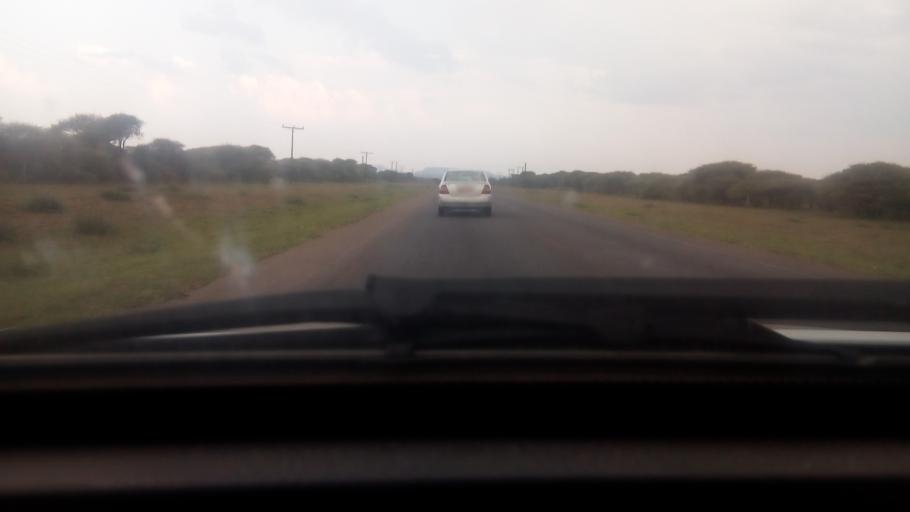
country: BW
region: Kweneng
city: Metsemotlhaba
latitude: -24.5226
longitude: 25.7631
